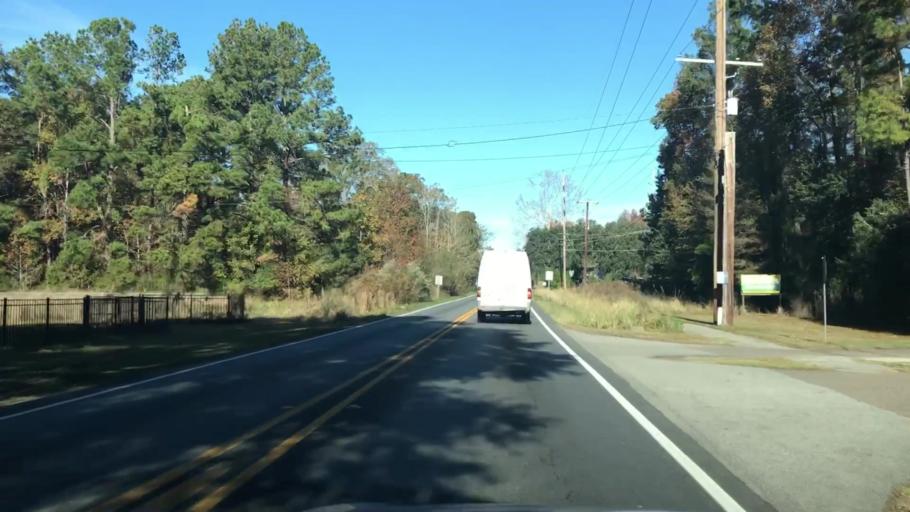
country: US
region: South Carolina
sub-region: Dorchester County
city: Summerville
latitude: 33.0030
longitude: -80.2330
